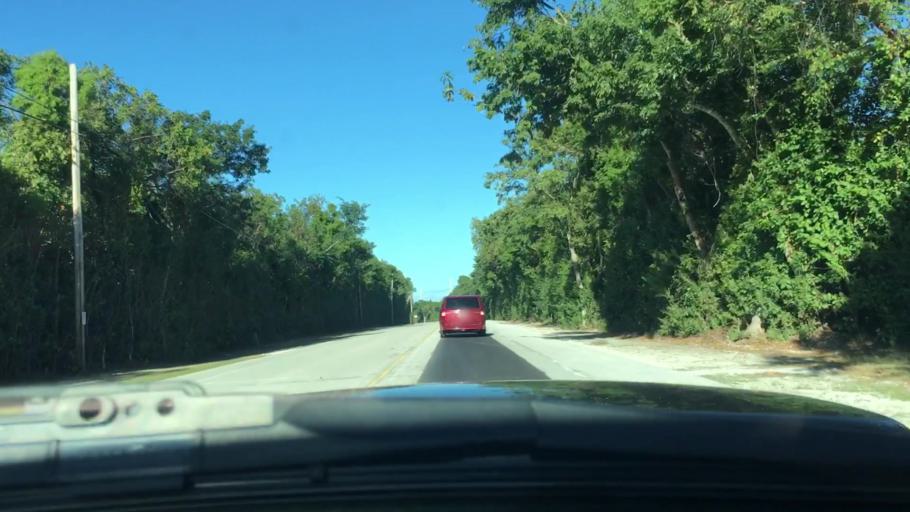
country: US
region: Florida
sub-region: Monroe County
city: North Key Largo
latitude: 25.2043
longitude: -80.3449
